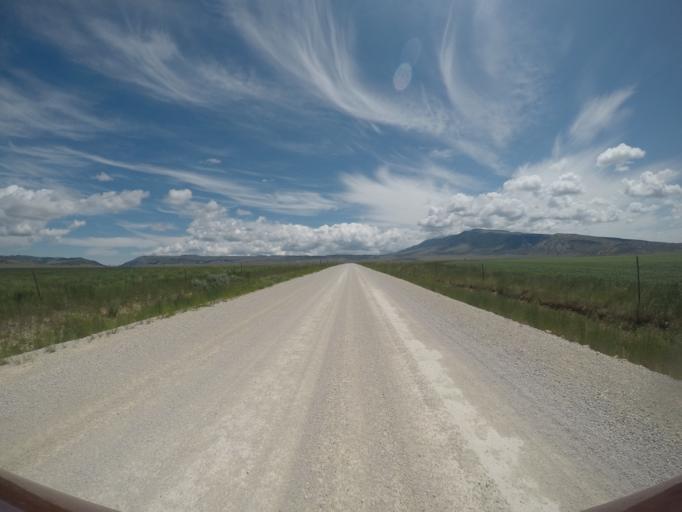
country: US
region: Montana
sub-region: Yellowstone County
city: Laurel
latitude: 45.2195
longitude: -108.7032
